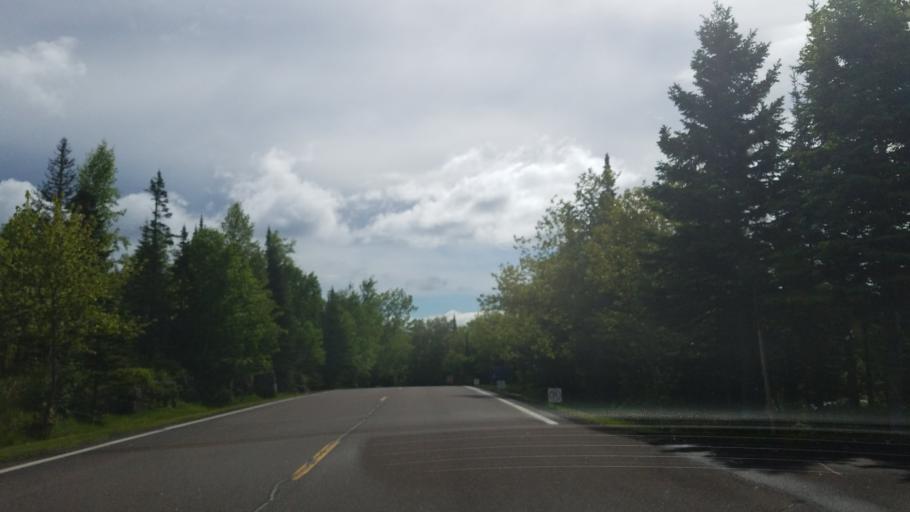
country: US
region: Minnesota
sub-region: Lake County
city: Silver Bay
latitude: 47.2020
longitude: -91.3692
